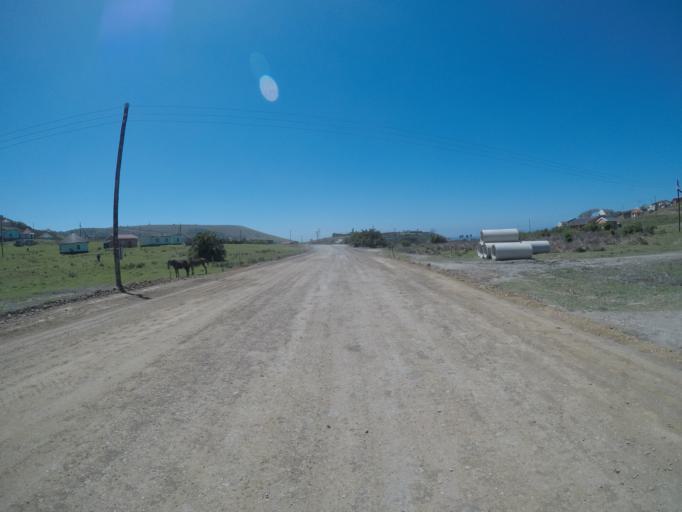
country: ZA
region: Eastern Cape
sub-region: OR Tambo District Municipality
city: Libode
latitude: -32.0313
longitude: 29.1062
